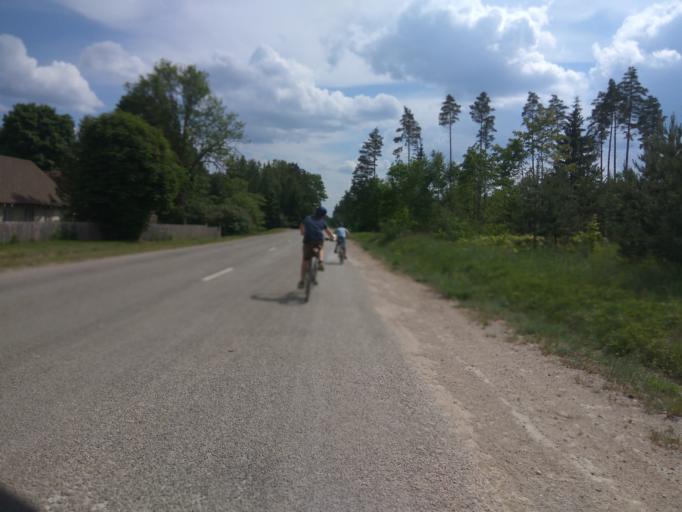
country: LV
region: Kuldigas Rajons
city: Kuldiga
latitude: 56.9054
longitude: 21.9373
